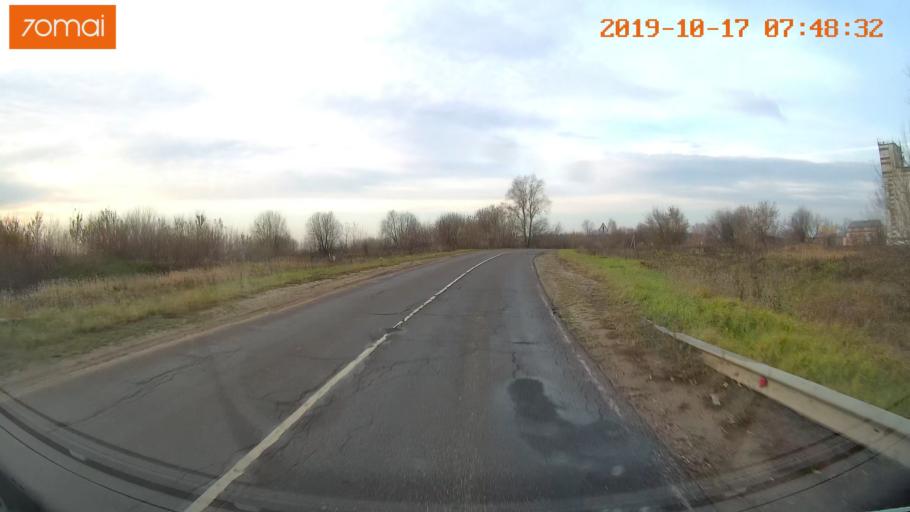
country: RU
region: Vladimir
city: Yur'yev-Pol'skiy
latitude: 56.4791
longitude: 39.6749
